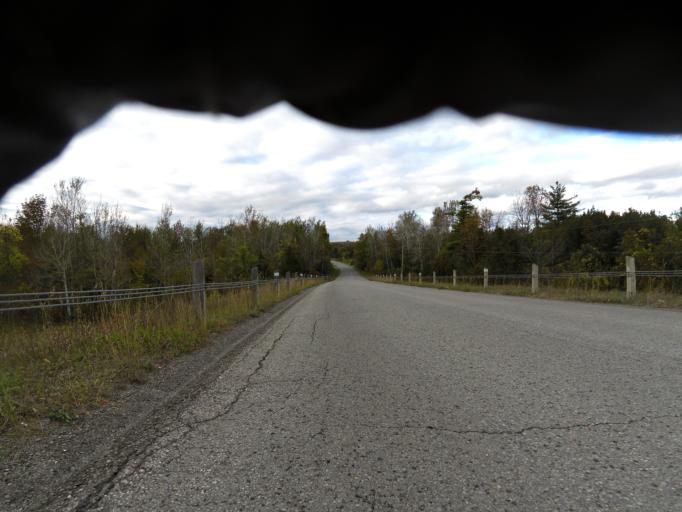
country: CA
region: Ontario
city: Cobourg
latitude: 43.9728
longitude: -78.0635
